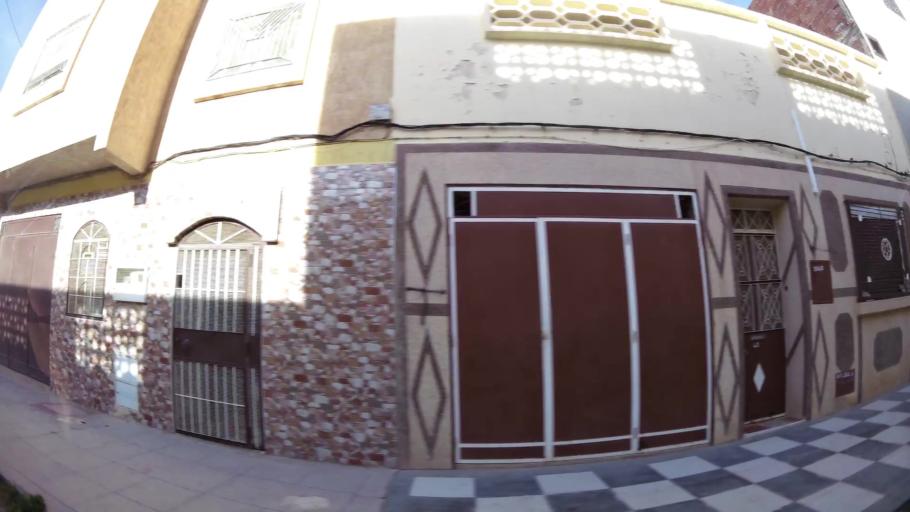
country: MA
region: Oriental
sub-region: Oujda-Angad
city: Oujda
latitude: 34.6739
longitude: -1.8960
